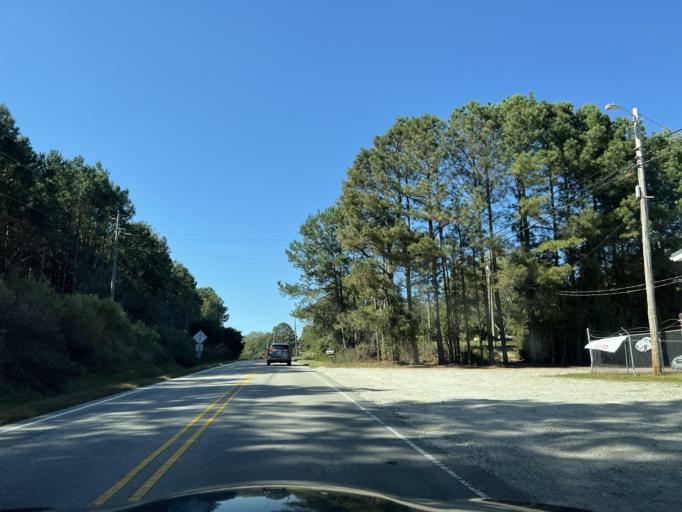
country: US
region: North Carolina
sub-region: Wake County
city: Garner
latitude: 35.6917
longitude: -78.5455
